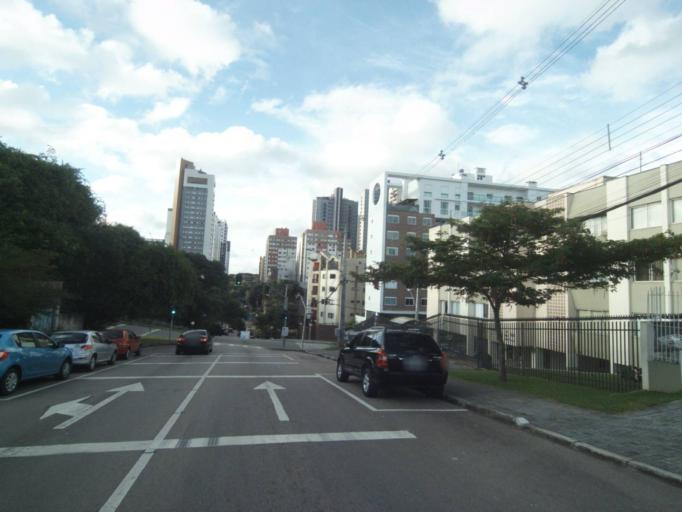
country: BR
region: Parana
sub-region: Curitiba
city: Curitiba
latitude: -25.4370
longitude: -49.3020
